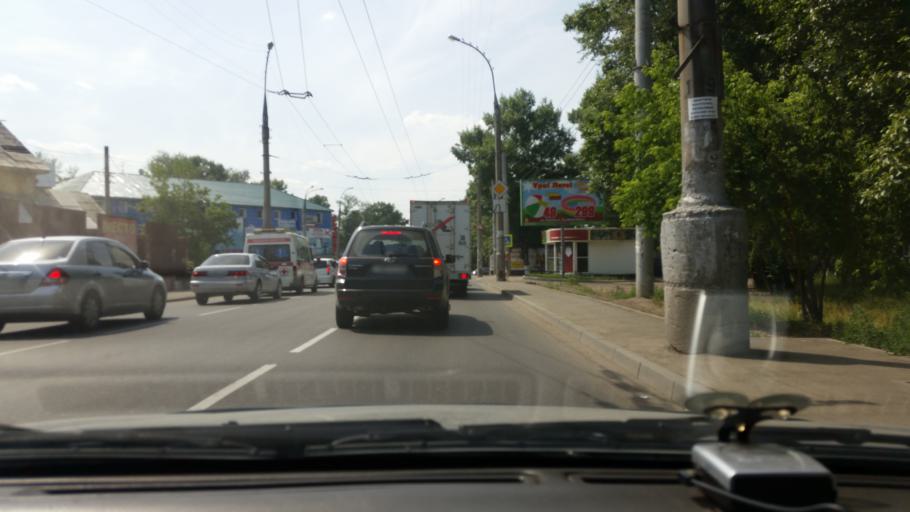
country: RU
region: Irkutsk
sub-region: Irkutskiy Rayon
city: Irkutsk
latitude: 52.2295
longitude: 104.3099
